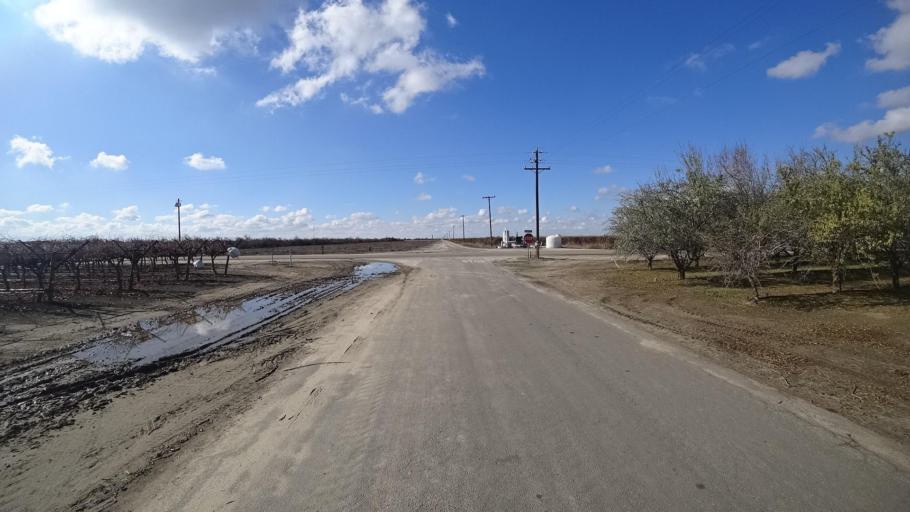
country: US
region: California
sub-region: Kern County
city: Delano
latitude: 35.7467
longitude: -119.3653
